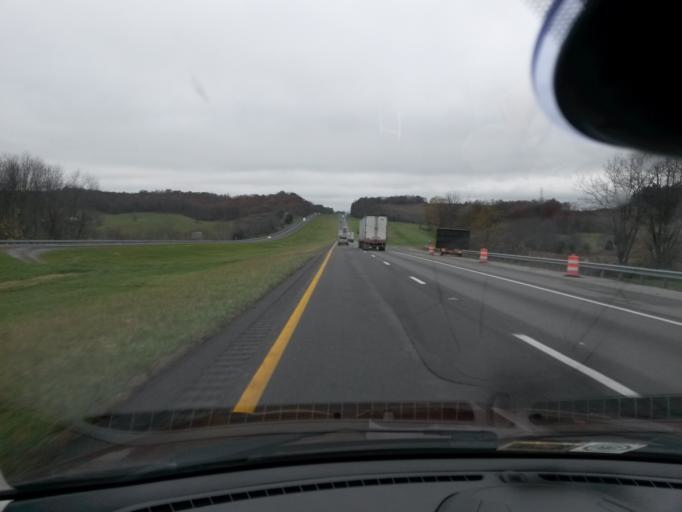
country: US
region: Virginia
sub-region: Pulaski County
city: Pulaski
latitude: 36.9088
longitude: -80.8843
